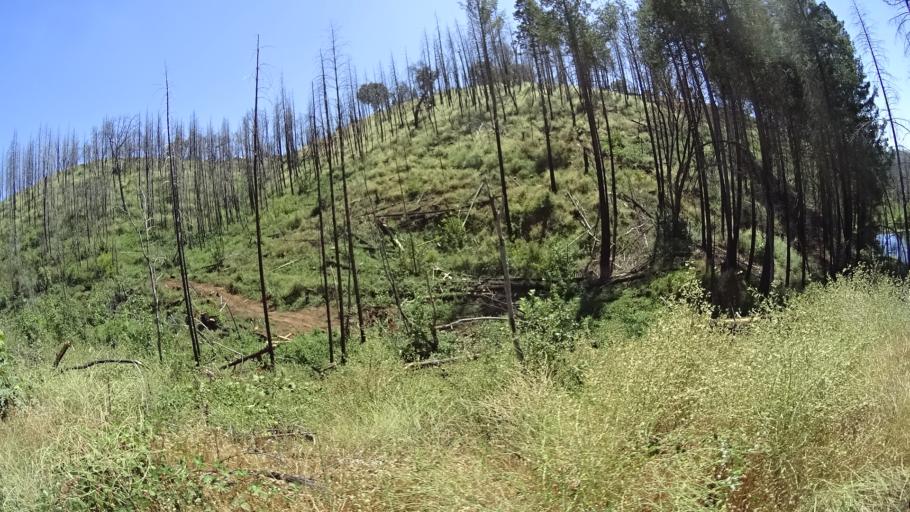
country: US
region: California
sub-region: Calaveras County
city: Mountain Ranch
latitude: 38.2901
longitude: -120.5369
